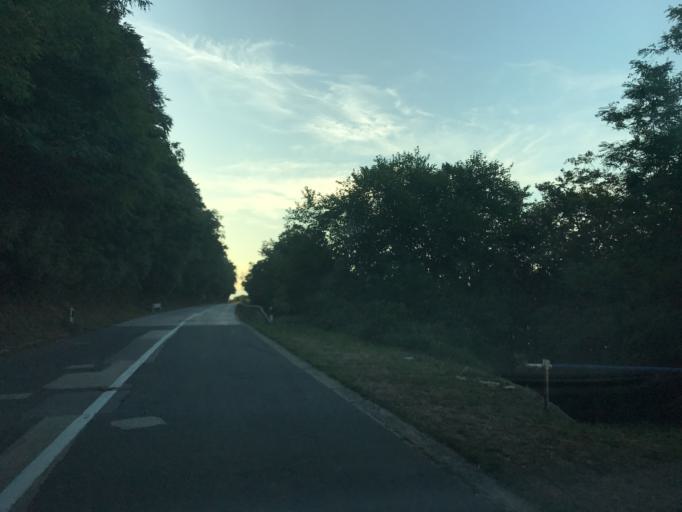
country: RO
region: Caras-Severin
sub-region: Comuna Berzasca
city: Berzasca
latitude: 44.6317
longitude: 21.9498
